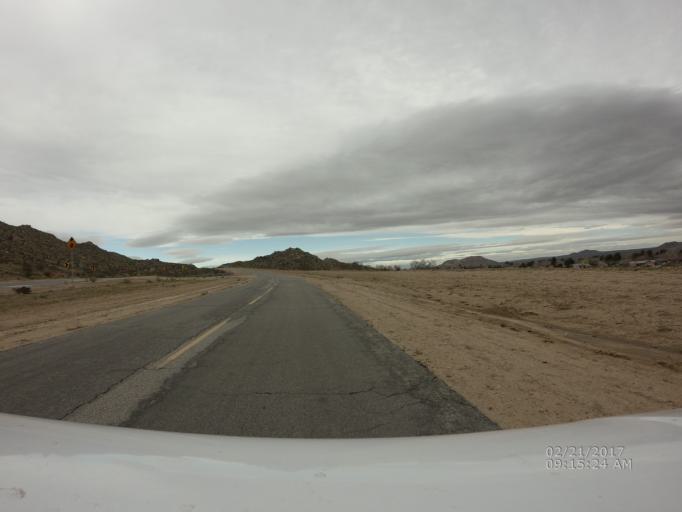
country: US
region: California
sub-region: Los Angeles County
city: Lake Los Angeles
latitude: 34.6072
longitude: -117.8338
